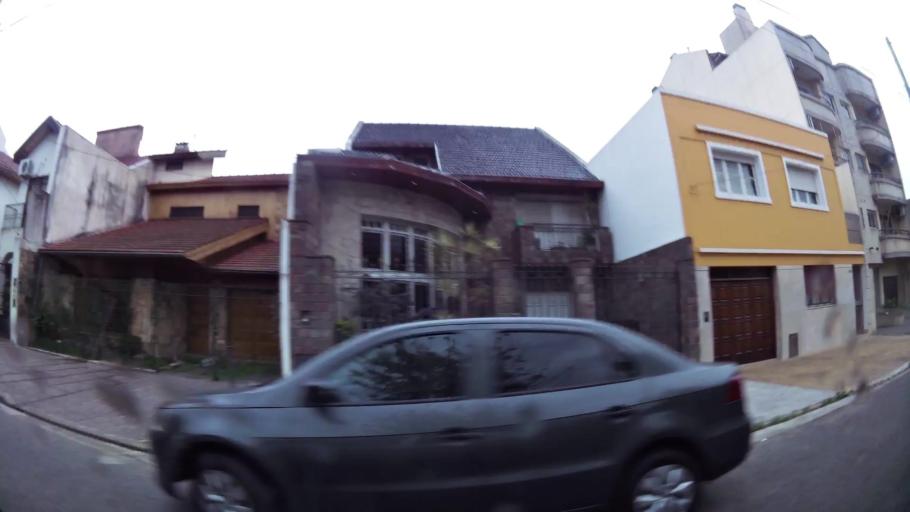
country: AR
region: Buenos Aires
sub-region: Partido de Lanus
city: Lanus
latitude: -34.7031
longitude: -58.3992
